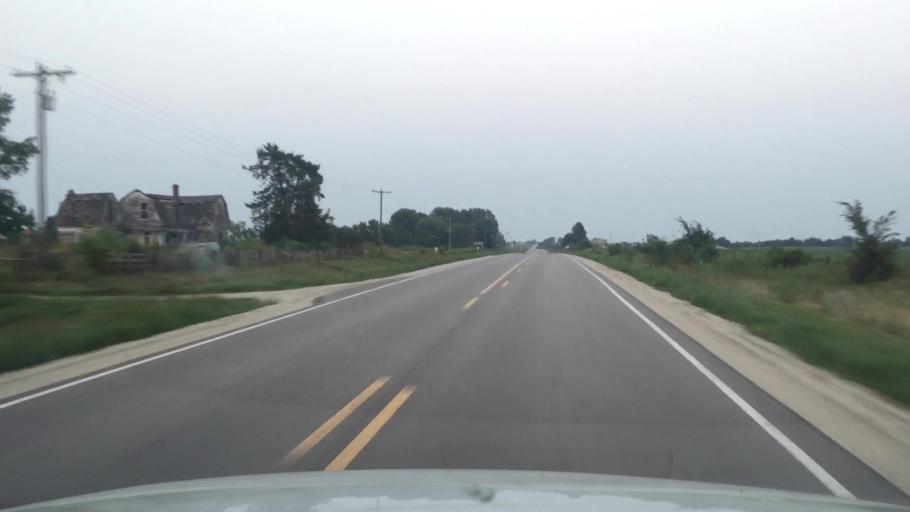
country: US
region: Iowa
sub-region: Warren County
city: Indianola
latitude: 41.1825
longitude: -93.4798
